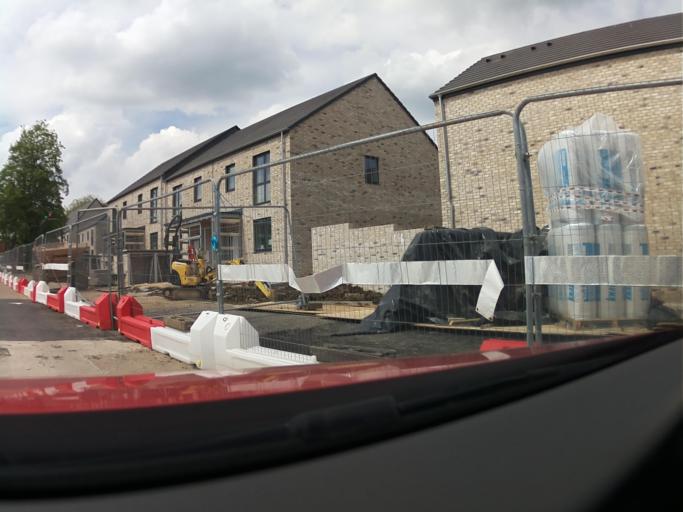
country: GB
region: England
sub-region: Bristol
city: Bristol
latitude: 51.5070
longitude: -2.6016
